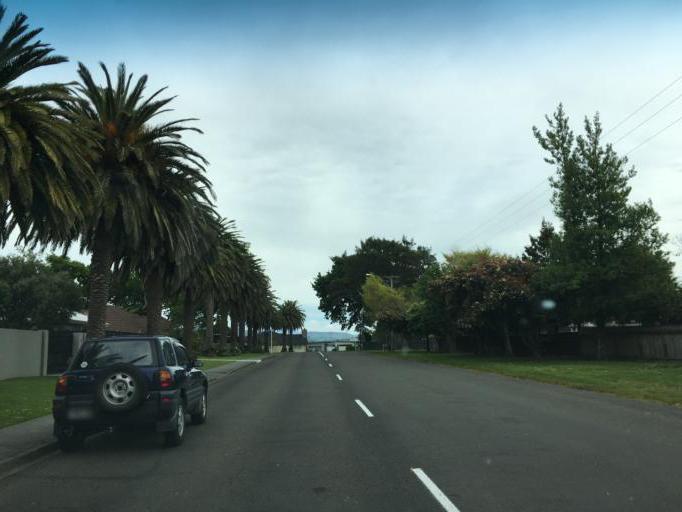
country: NZ
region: Manawatu-Wanganui
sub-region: Palmerston North City
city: Palmerston North
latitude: -40.3779
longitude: 175.5786
